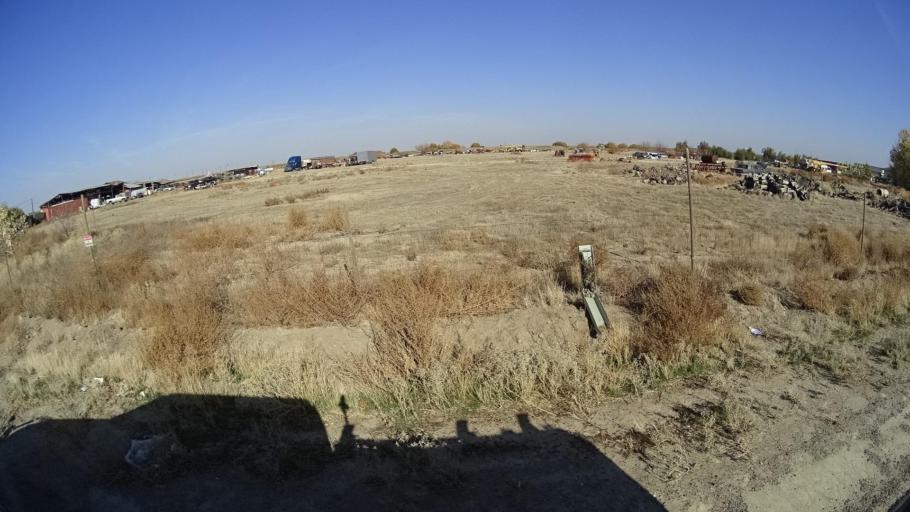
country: US
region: California
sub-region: Kern County
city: Wasco
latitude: 35.7178
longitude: -119.3895
